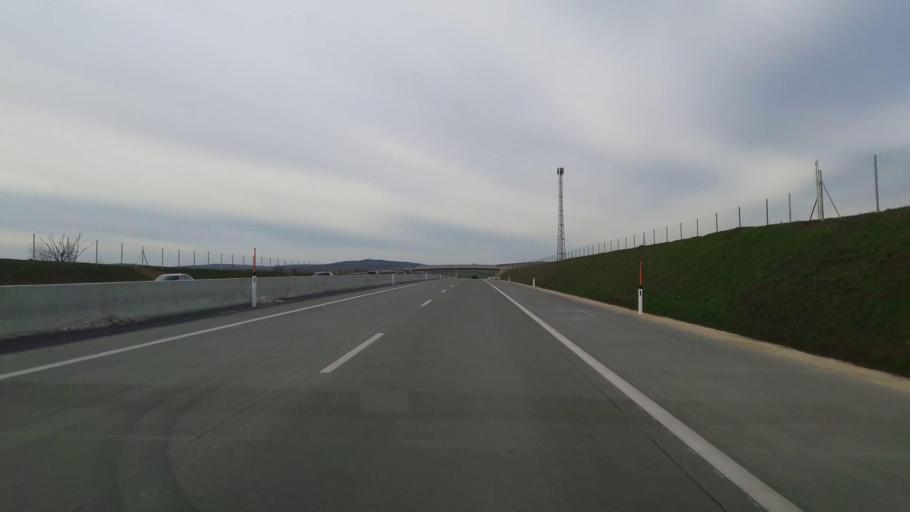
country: AT
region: Lower Austria
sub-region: Politischer Bezirk Mistelbach
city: Herrnbaumgarten
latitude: 48.6757
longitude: 16.6698
